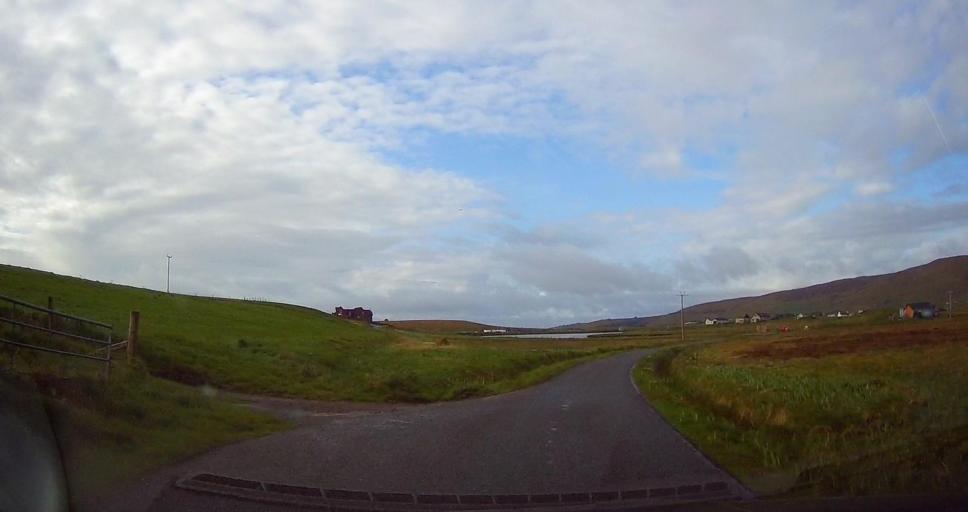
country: GB
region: Scotland
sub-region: Shetland Islands
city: Sandwick
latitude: 60.0482
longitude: -1.2069
